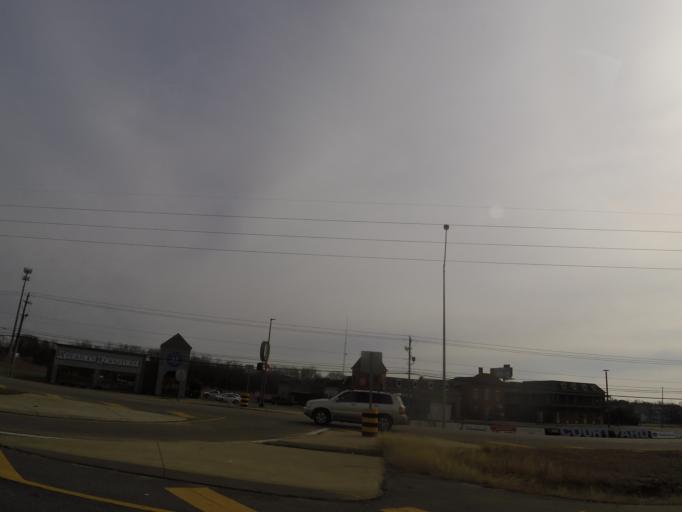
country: US
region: Alabama
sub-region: Montgomery County
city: Montgomery
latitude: 32.3522
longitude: -86.2198
